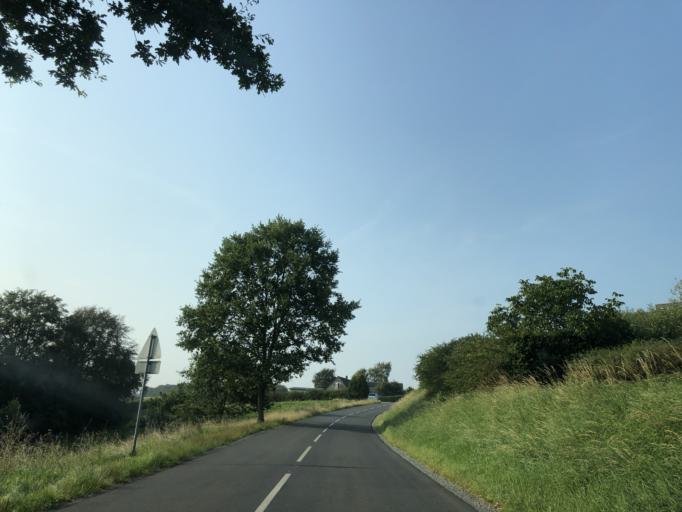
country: DK
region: Central Jutland
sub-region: Favrskov Kommune
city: Hammel
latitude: 56.2347
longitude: 9.7413
